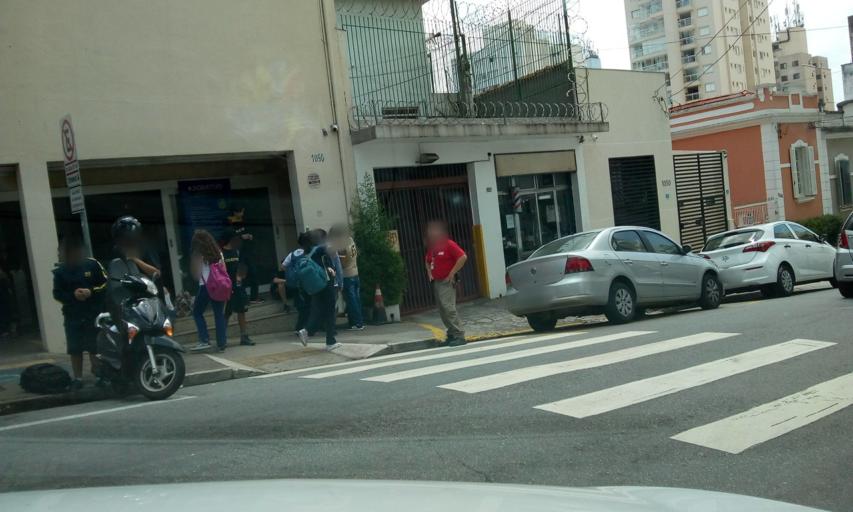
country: BR
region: Sao Paulo
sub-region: Sao Paulo
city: Sao Paulo
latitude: -23.5701
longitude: -46.6378
